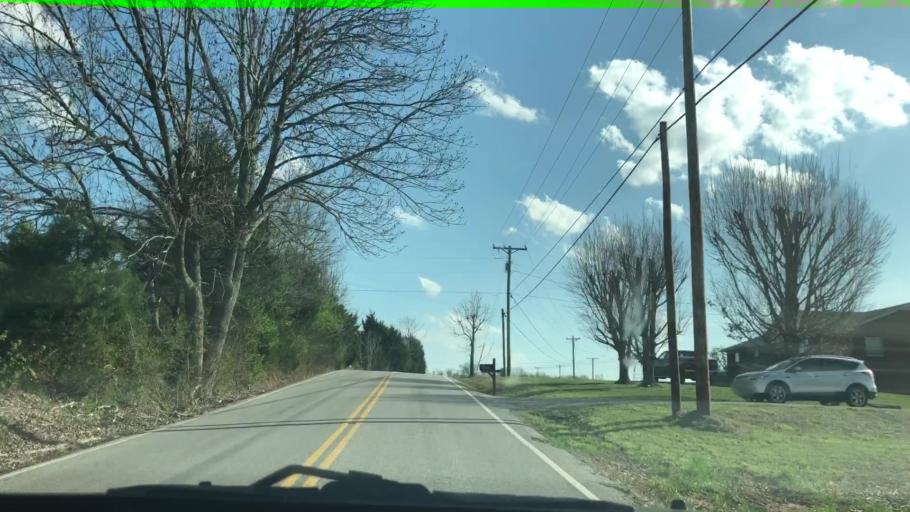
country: US
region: Tennessee
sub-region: Putnam County
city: Baxter
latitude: 36.0828
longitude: -85.5851
